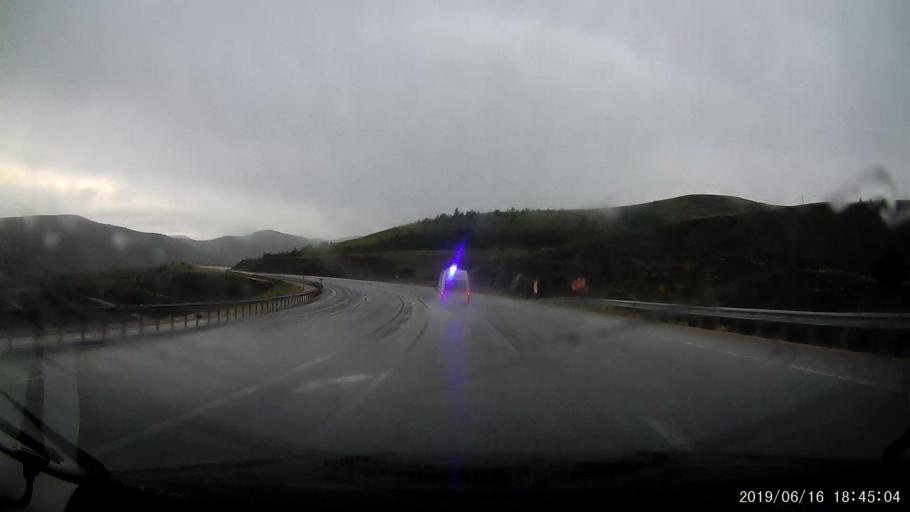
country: TR
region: Erzincan
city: Doganbeyli
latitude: 39.8723
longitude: 39.0634
